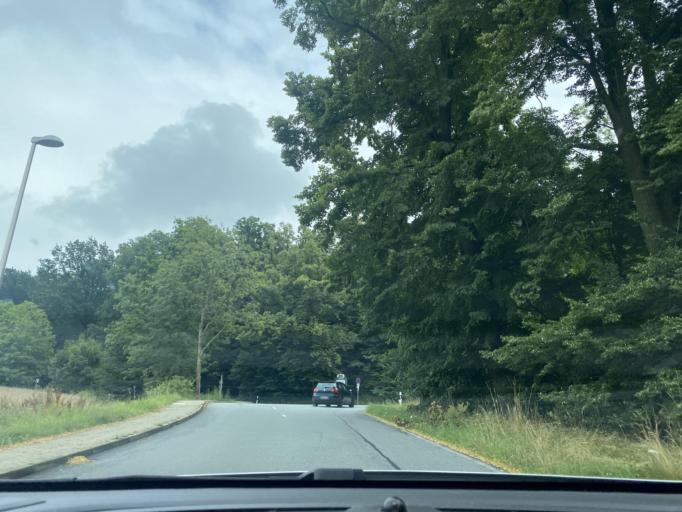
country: DE
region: Saxony
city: Lobau
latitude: 51.0946
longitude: 14.6817
